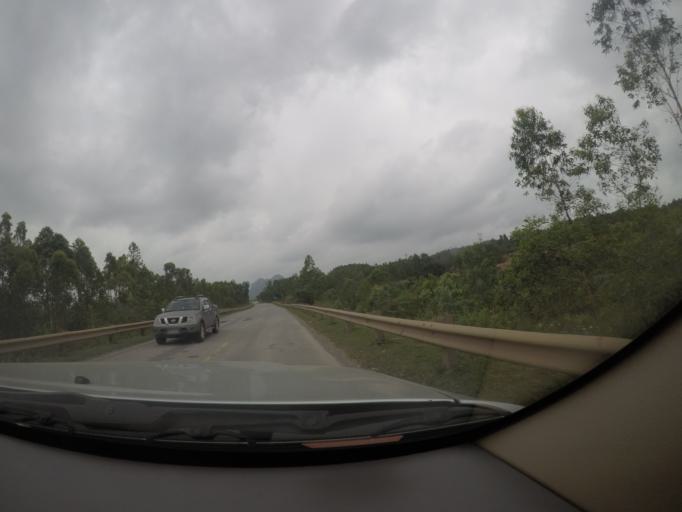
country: VN
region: Quang Binh
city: Quan Hau
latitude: 17.3292
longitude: 106.6244
